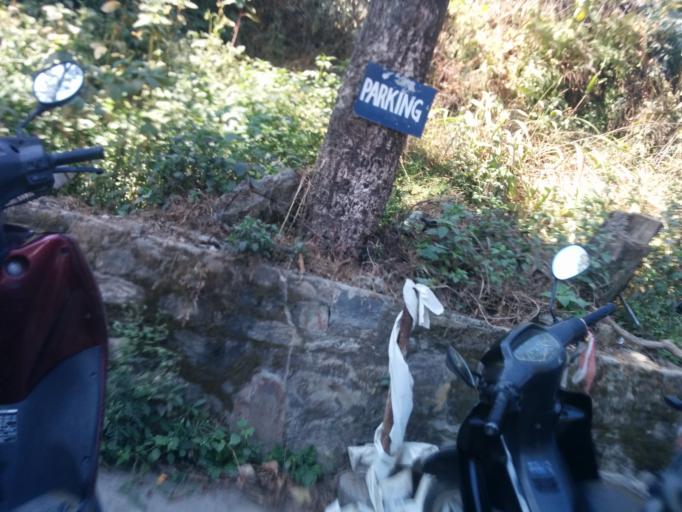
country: NP
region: Central Region
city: Kirtipur
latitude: 27.6826
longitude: 85.2734
